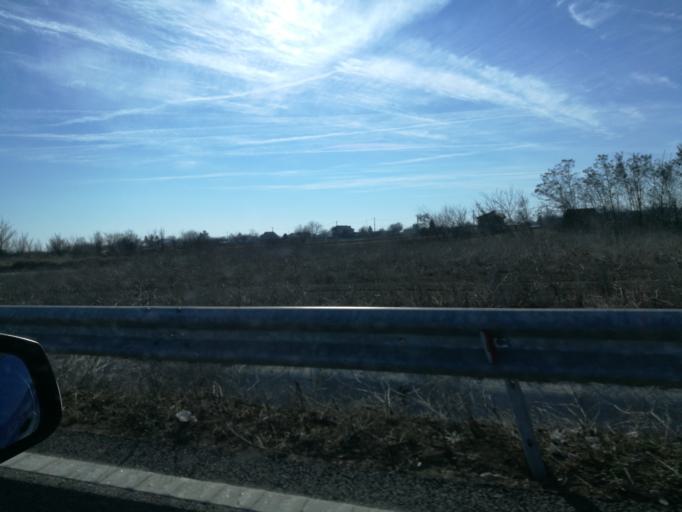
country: RO
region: Ilfov
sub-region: Comuna Moara Vlasiei
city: Caciulati
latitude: 44.6326
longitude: 26.1835
